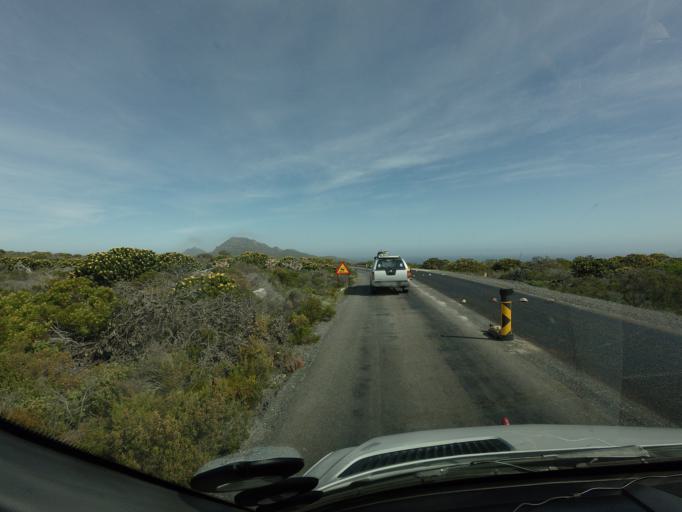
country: ZA
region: Western Cape
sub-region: City of Cape Town
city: Retreat
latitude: -34.3272
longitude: 18.4570
